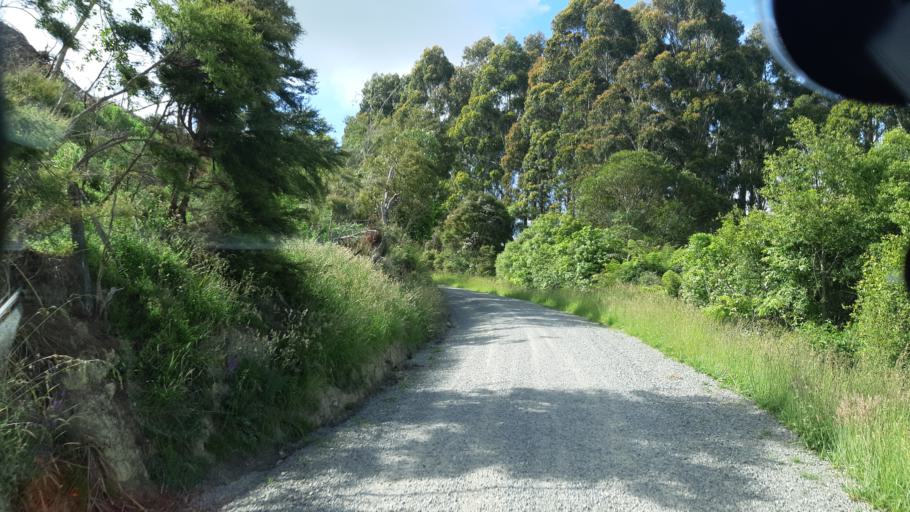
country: NZ
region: Manawatu-Wanganui
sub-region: Rangitikei District
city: Bulls
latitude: -39.9603
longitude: 175.4740
